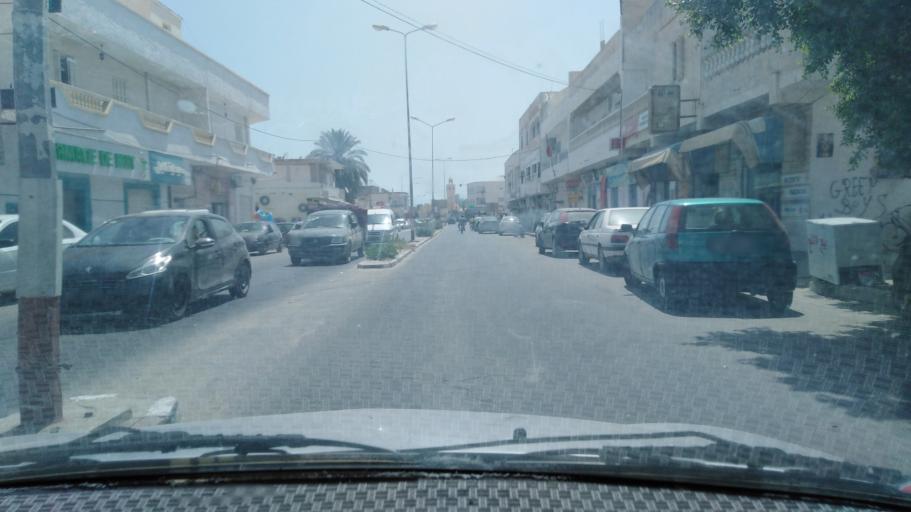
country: TN
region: Qabis
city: Gabes
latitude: 33.9595
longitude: 10.0001
